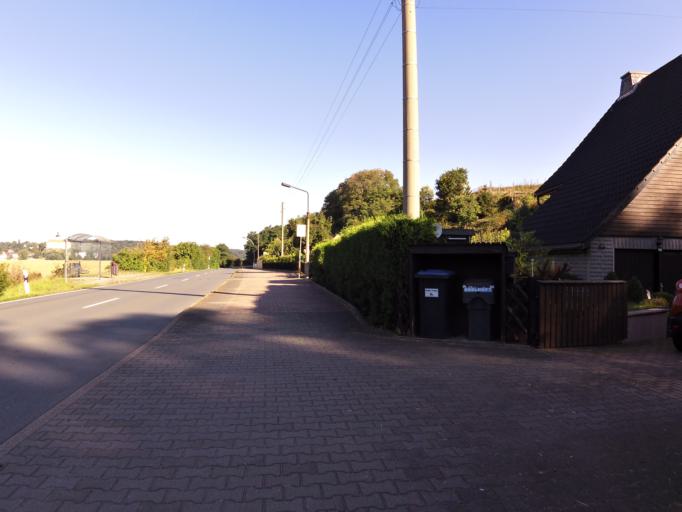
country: DE
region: Saxony
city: Weissig
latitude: 51.2455
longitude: 13.4136
